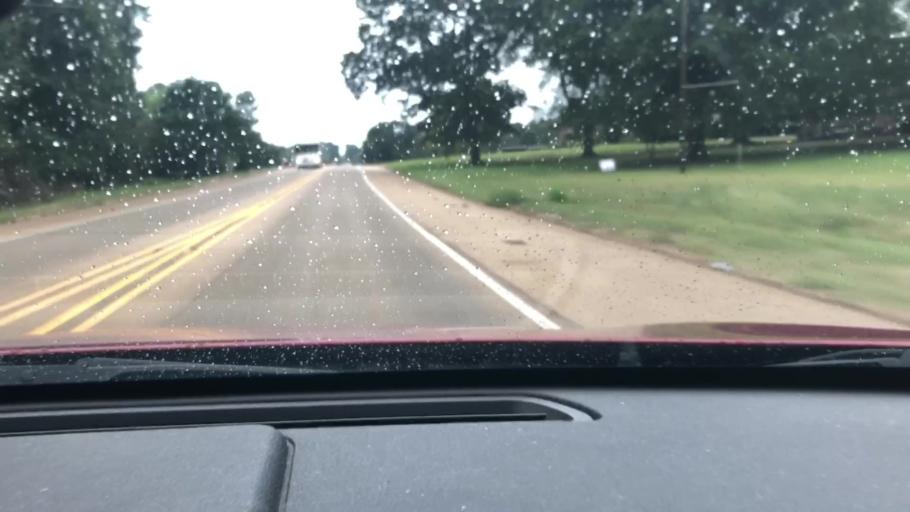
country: US
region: Arkansas
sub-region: Lafayette County
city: Stamps
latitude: 33.3650
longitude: -93.4810
